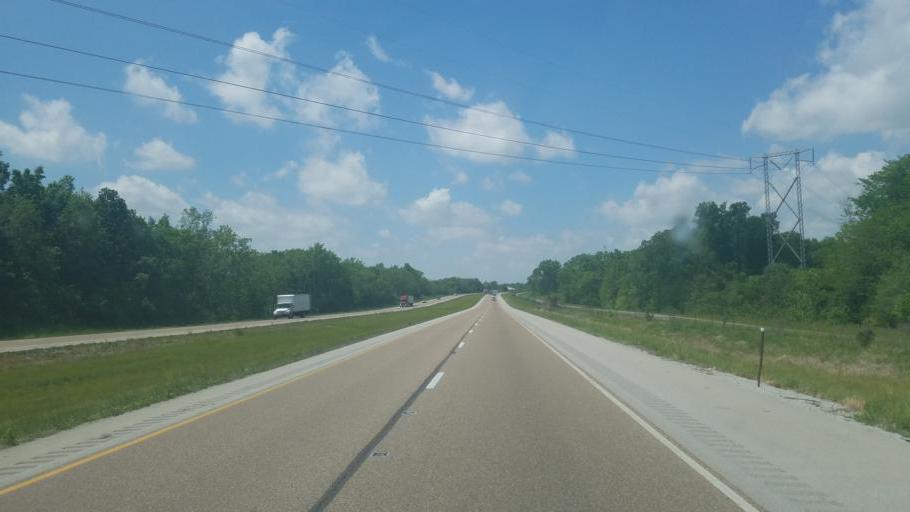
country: US
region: Illinois
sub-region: Cumberland County
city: Greenup
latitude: 39.2670
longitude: -88.1197
